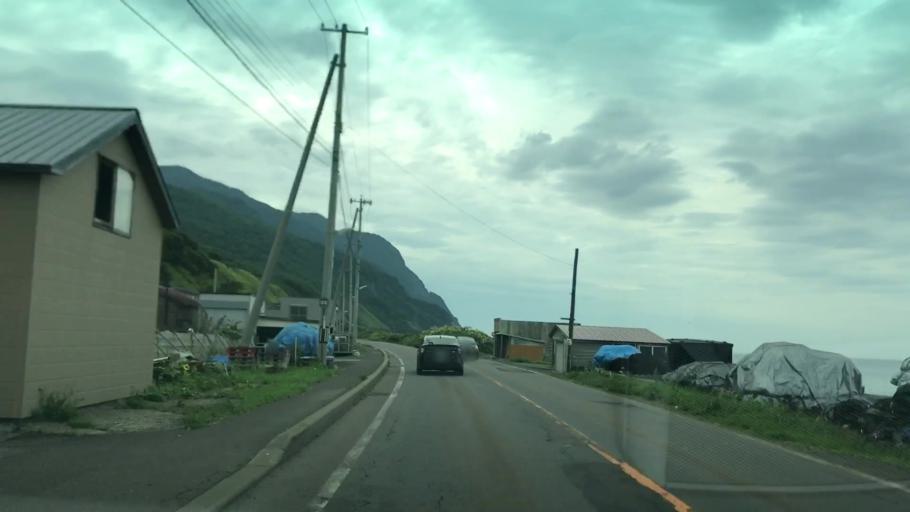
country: JP
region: Hokkaido
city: Iwanai
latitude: 42.9661
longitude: 140.4708
